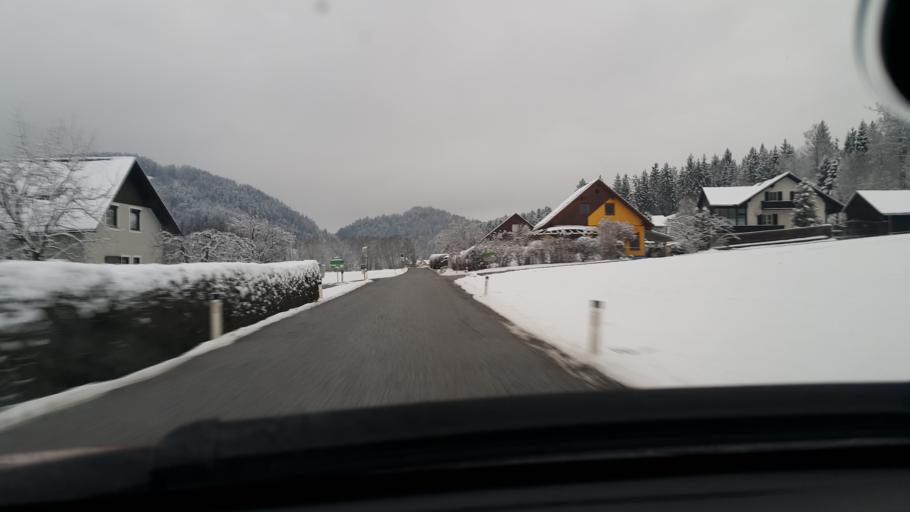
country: AT
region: Styria
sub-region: Politischer Bezirk Graz-Umgebung
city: Sankt Oswald bei Plankenwarth
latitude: 47.0781
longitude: 15.2621
